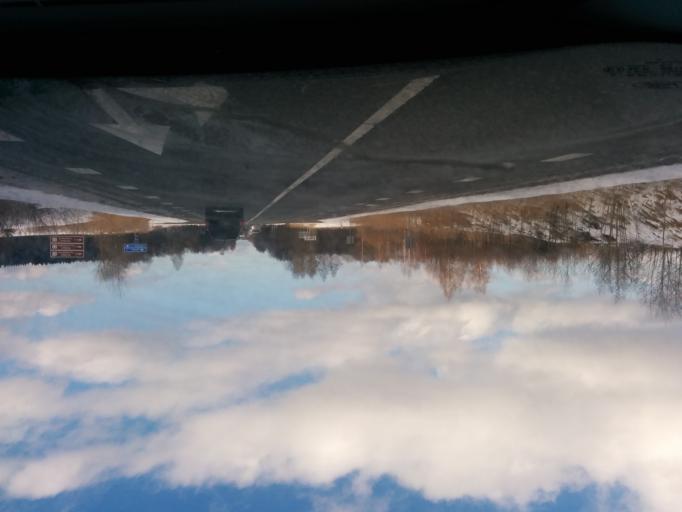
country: LV
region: Raunas
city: Rauna
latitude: 57.3076
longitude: 25.6262
